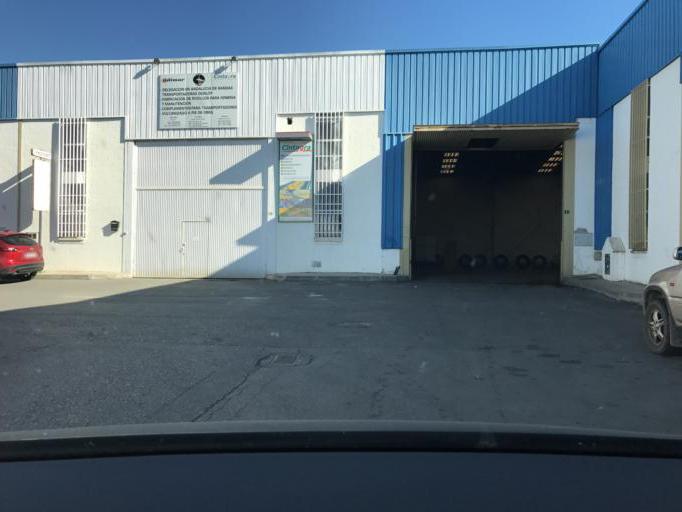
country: ES
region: Andalusia
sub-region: Provincia de Granada
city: Peligros
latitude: 37.2252
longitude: -3.6369
